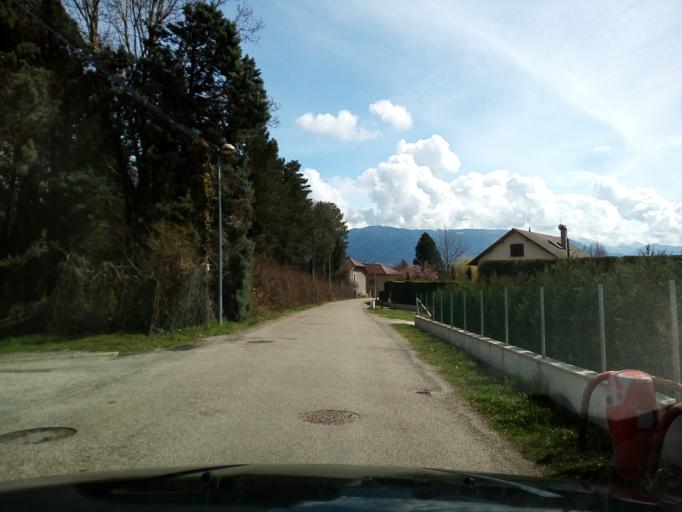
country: FR
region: Rhone-Alpes
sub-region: Departement de l'Isere
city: Chapareillan
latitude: 45.4730
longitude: 5.9855
